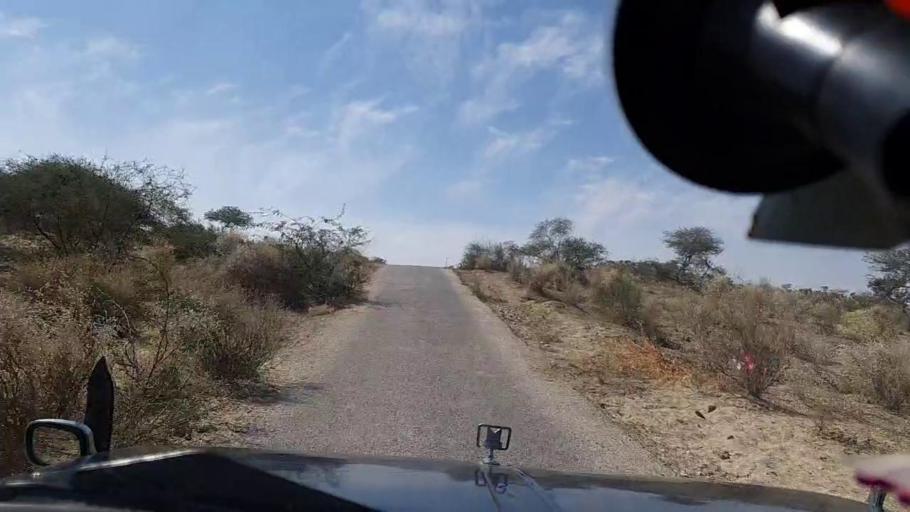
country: PK
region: Sindh
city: Diplo
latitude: 24.3858
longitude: 69.5873
